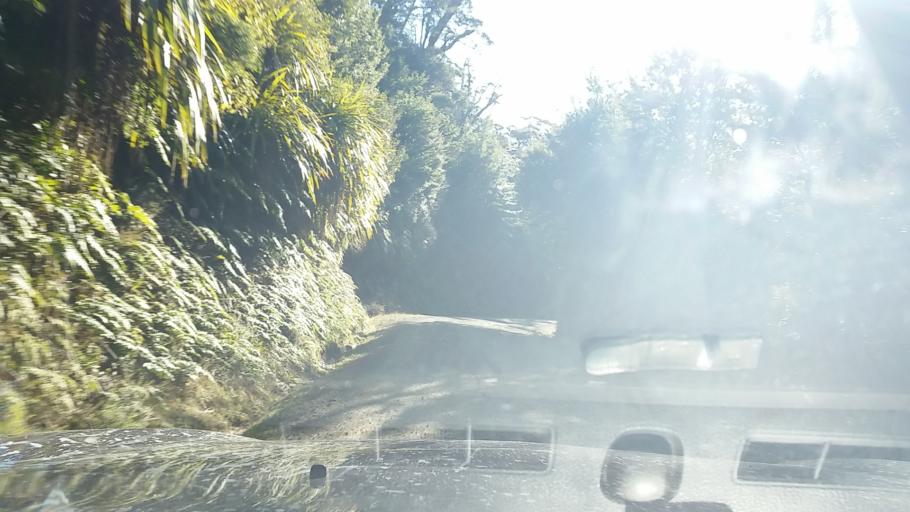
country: NZ
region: Marlborough
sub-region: Marlborough District
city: Picton
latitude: -41.0606
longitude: 174.1600
